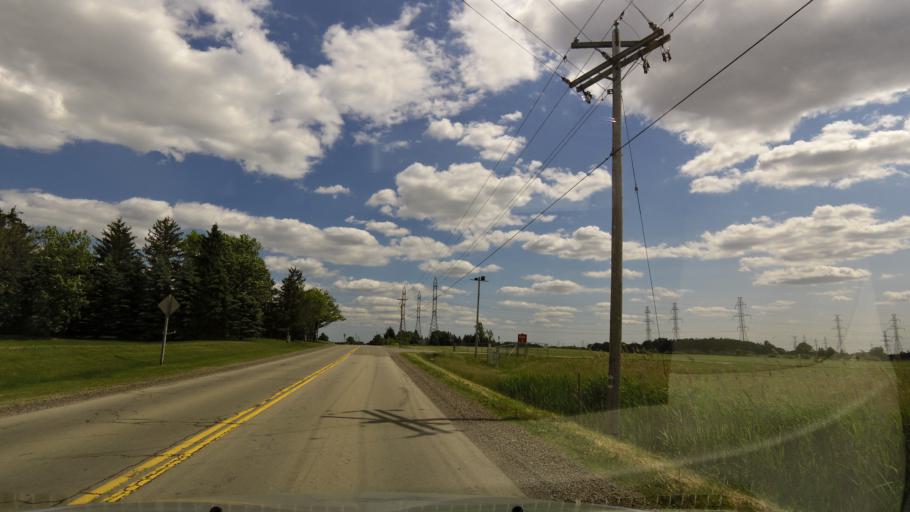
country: CA
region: Ontario
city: Ancaster
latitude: 43.1855
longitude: -80.0394
